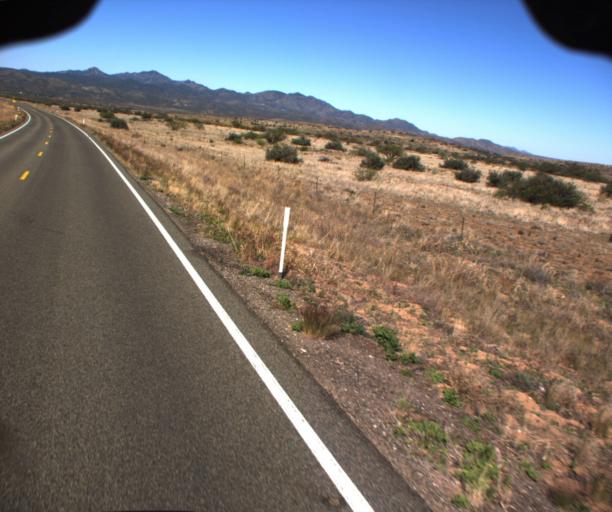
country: US
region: Arizona
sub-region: Yavapai County
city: Prescott
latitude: 34.3875
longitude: -112.6472
